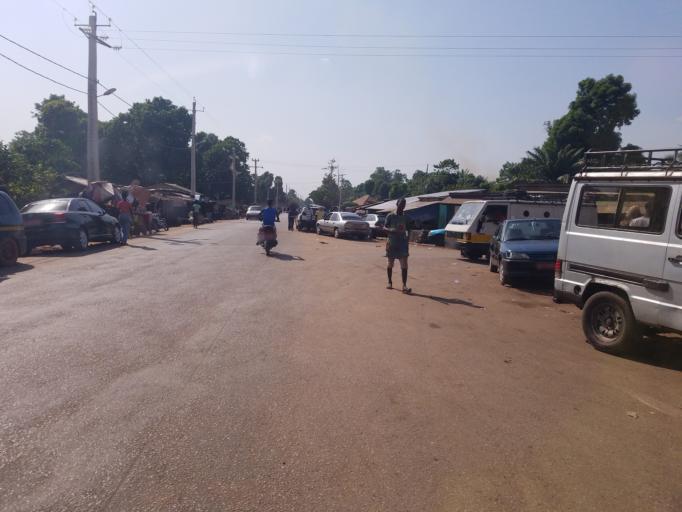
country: GN
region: Boke
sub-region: Fria
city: Fria
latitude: 10.0817
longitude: -13.6920
